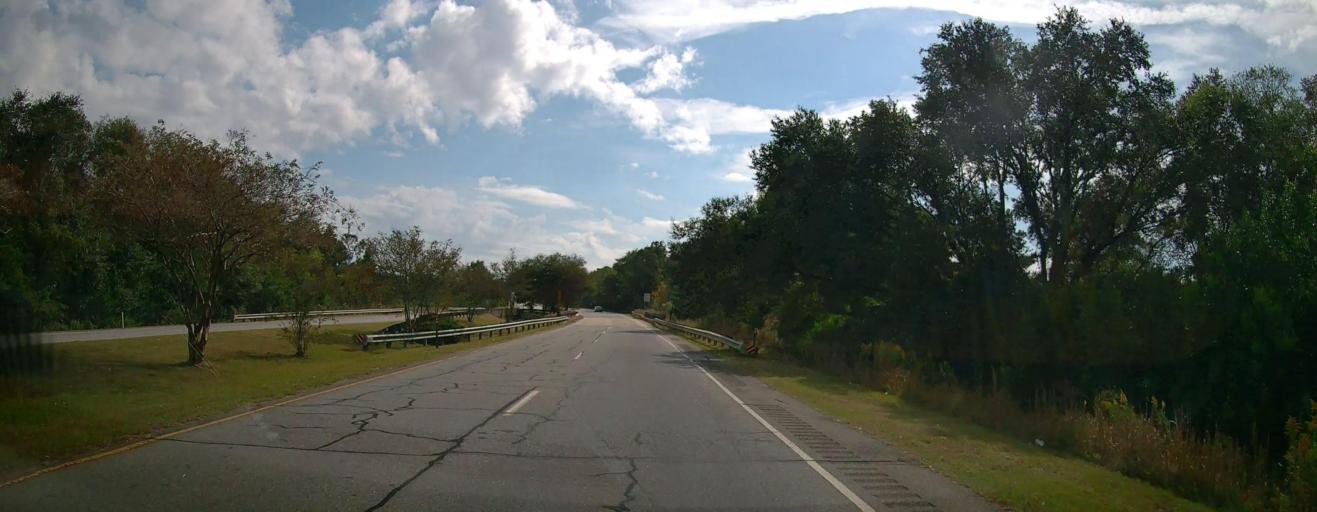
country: US
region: Georgia
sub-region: Mitchell County
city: Camilla
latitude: 31.2456
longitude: -84.1998
